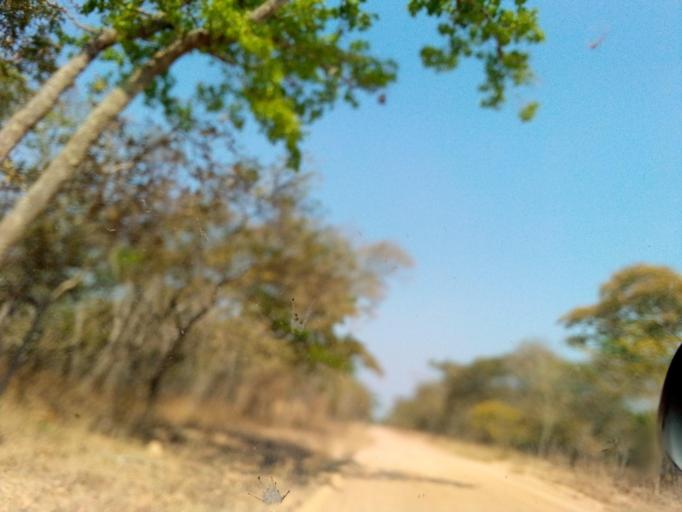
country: ZM
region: Northern
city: Mpika
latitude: -12.2421
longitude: 30.8456
